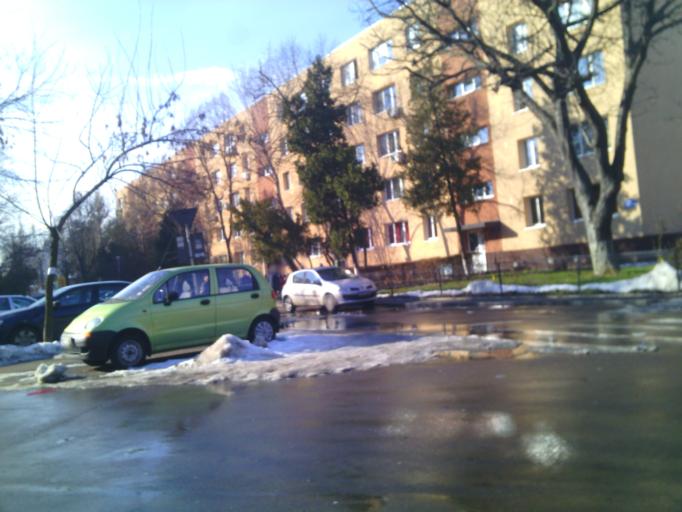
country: RO
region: Bucuresti
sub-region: Municipiul Bucuresti
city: Bucuresti
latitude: 44.3813
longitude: 26.1033
